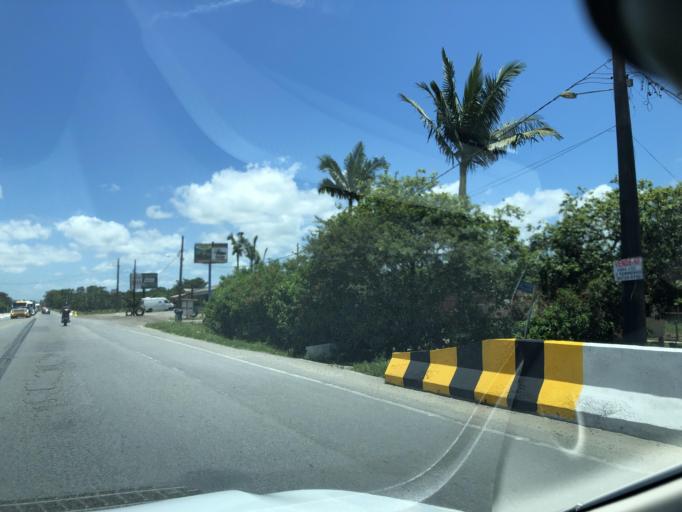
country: BR
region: Santa Catarina
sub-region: Joinville
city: Joinville
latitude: -26.4130
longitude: -48.7571
